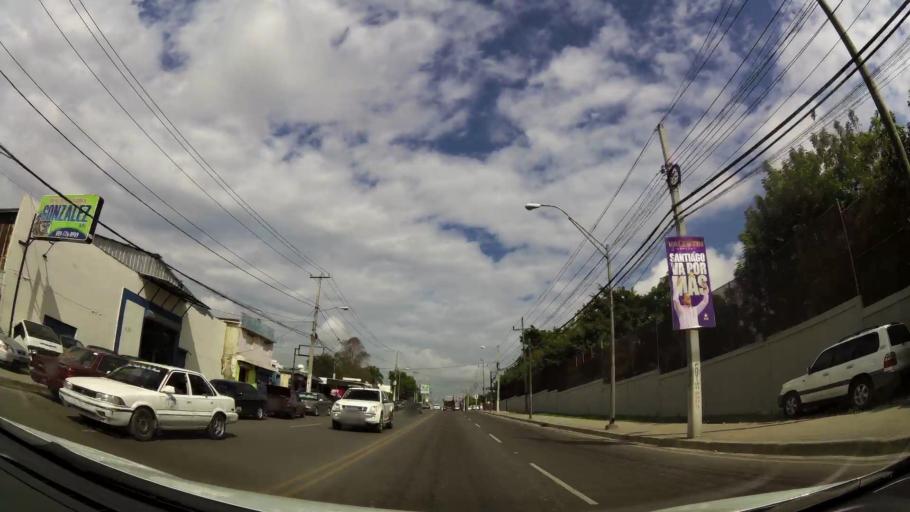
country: DO
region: Santiago
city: Santiago de los Caballeros
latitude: 19.4806
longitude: -70.7270
